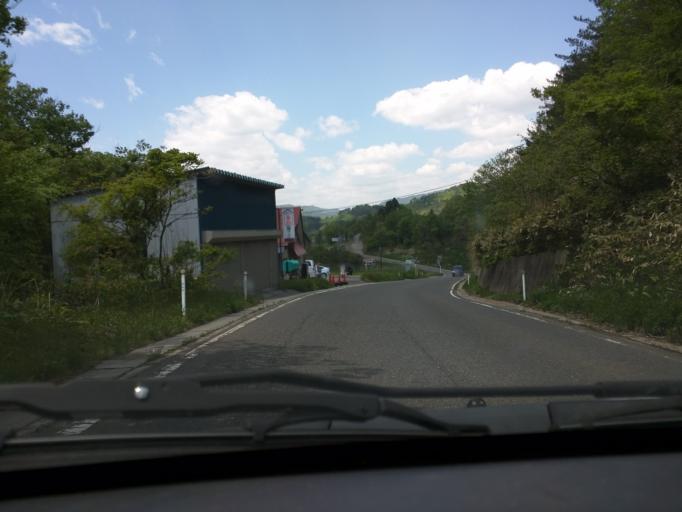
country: JP
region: Fukushima
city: Kitakata
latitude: 37.6389
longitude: 139.8000
